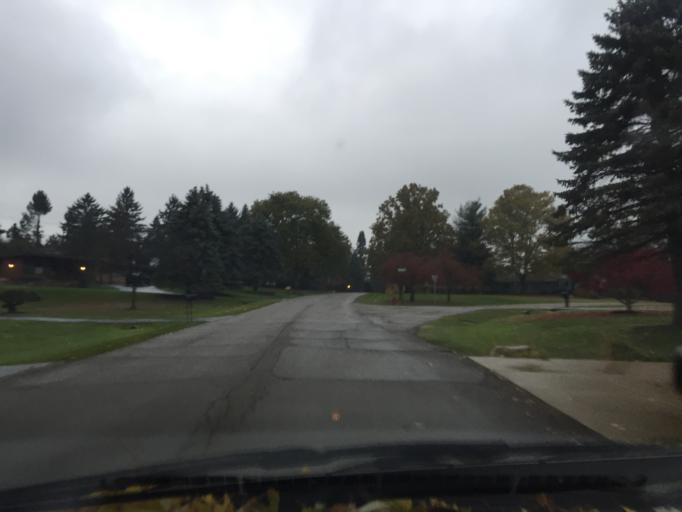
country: US
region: Michigan
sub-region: Oakland County
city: Bloomfield Hills
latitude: 42.5677
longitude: -83.2798
